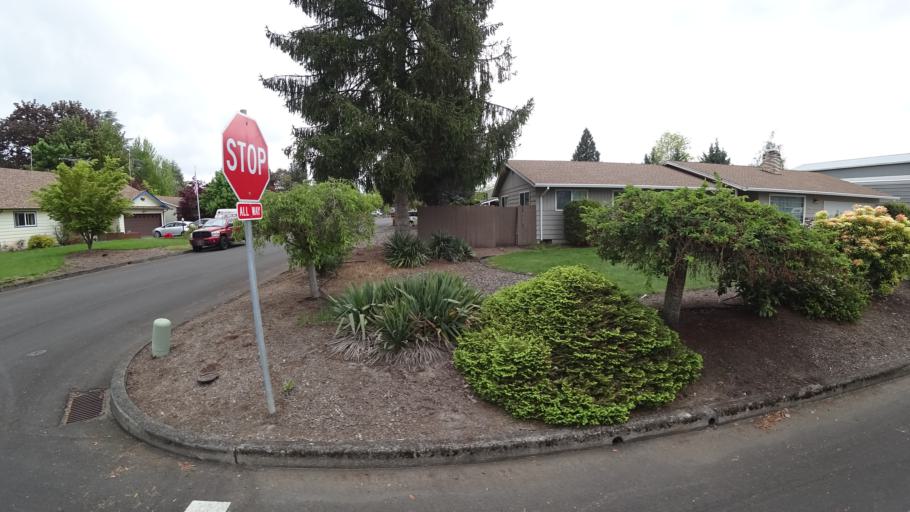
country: US
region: Oregon
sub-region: Washington County
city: Hillsboro
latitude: 45.5301
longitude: -122.9761
